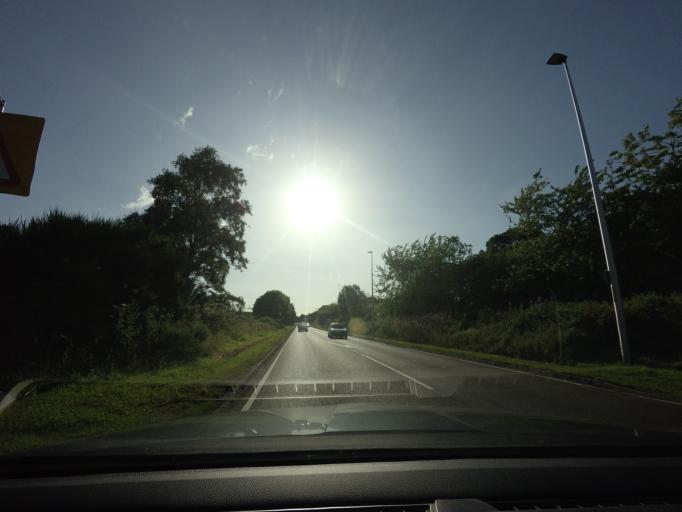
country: GB
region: Scotland
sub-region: Highland
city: Conon Bridge
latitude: 57.5405
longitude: -4.3376
